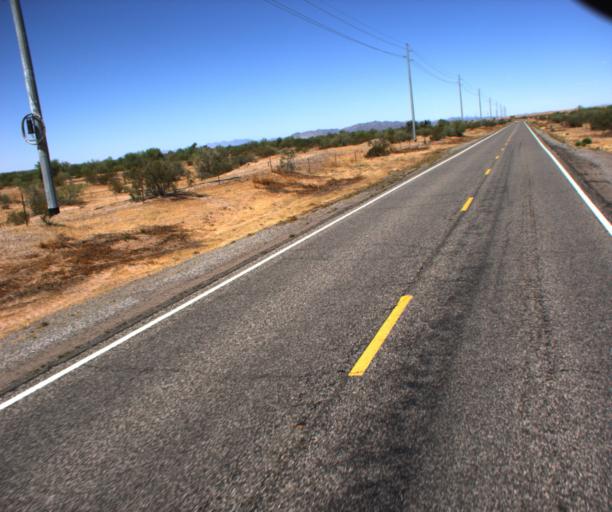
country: US
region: Arizona
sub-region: La Paz County
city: Cienega Springs
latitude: 33.9920
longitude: -114.0847
